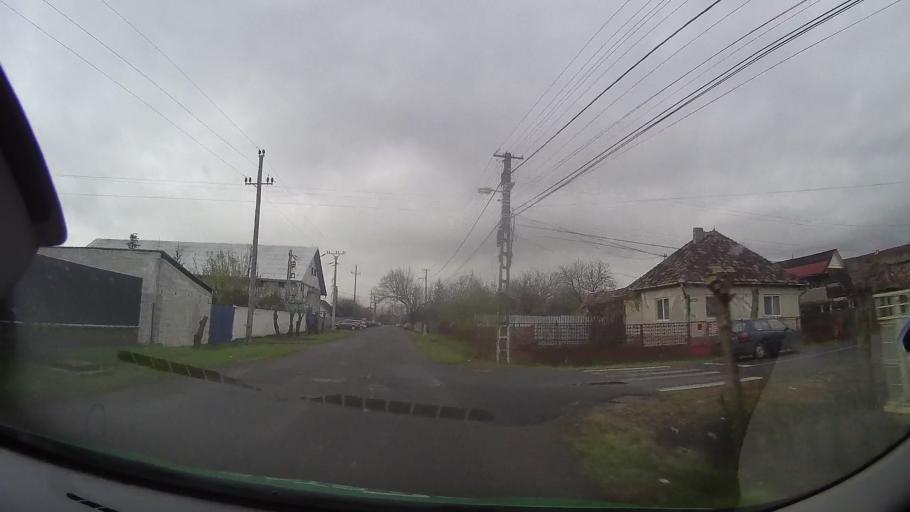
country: RO
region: Mures
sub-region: Municipiul Reghin
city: Iernuteni
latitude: 46.7742
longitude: 24.7229
